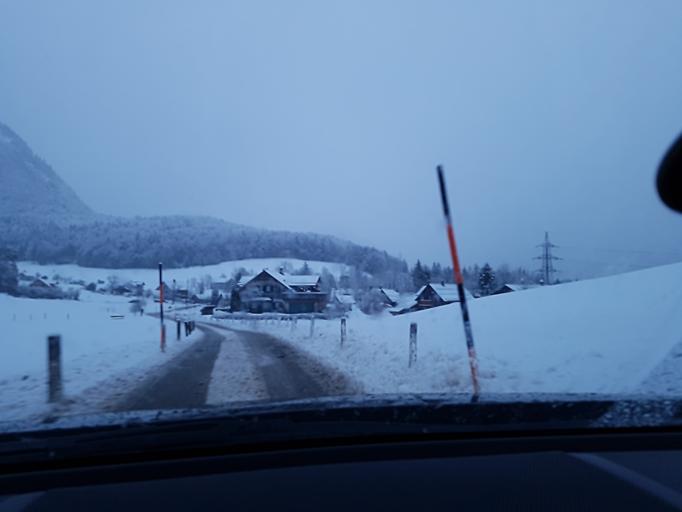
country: AT
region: Styria
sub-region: Politischer Bezirk Liezen
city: Altaussee
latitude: 47.6295
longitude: 13.7690
